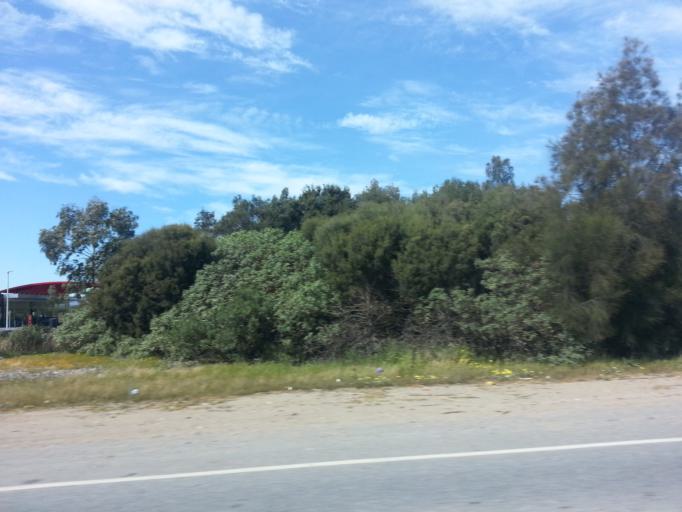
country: AU
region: South Australia
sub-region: Port Adelaide Enfield
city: Enfield
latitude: -34.8189
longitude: 138.5908
